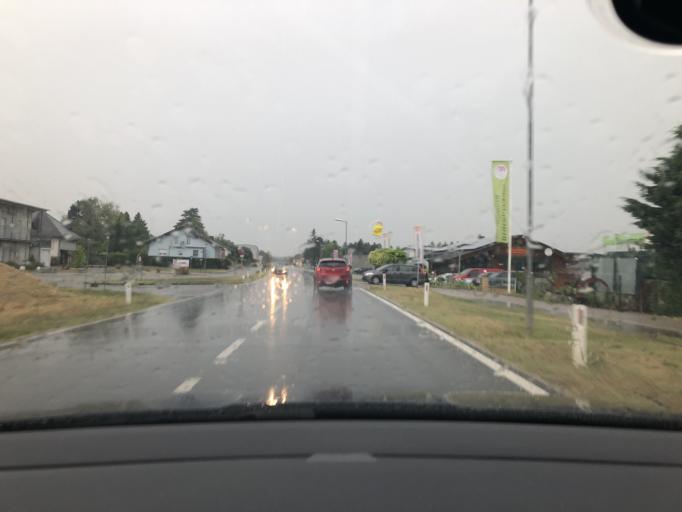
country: AT
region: Lower Austria
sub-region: Politischer Bezirk Ganserndorf
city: Marchegg
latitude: 48.2613
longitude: 16.9107
